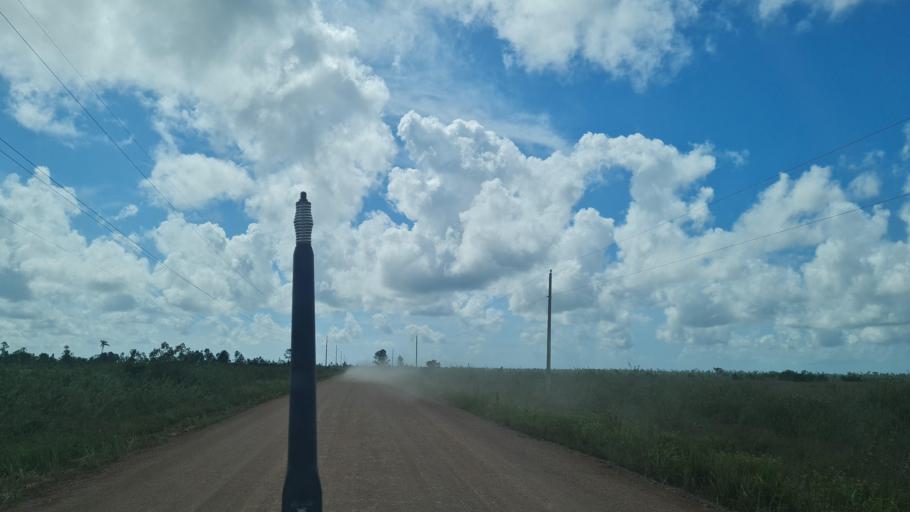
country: NI
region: Atlantico Norte (RAAN)
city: Puerto Cabezas
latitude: 14.1089
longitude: -83.5783
